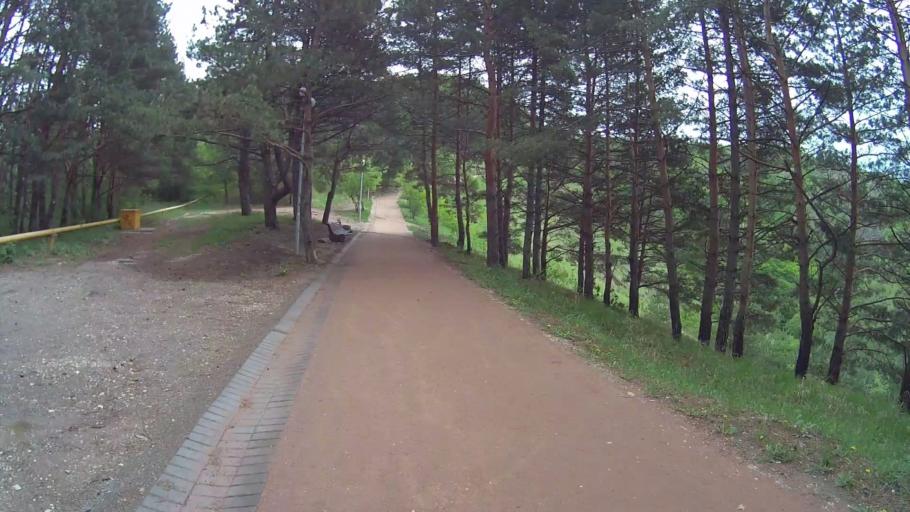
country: RU
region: Stavropol'skiy
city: Kislovodsk
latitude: 43.9001
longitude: 42.7529
